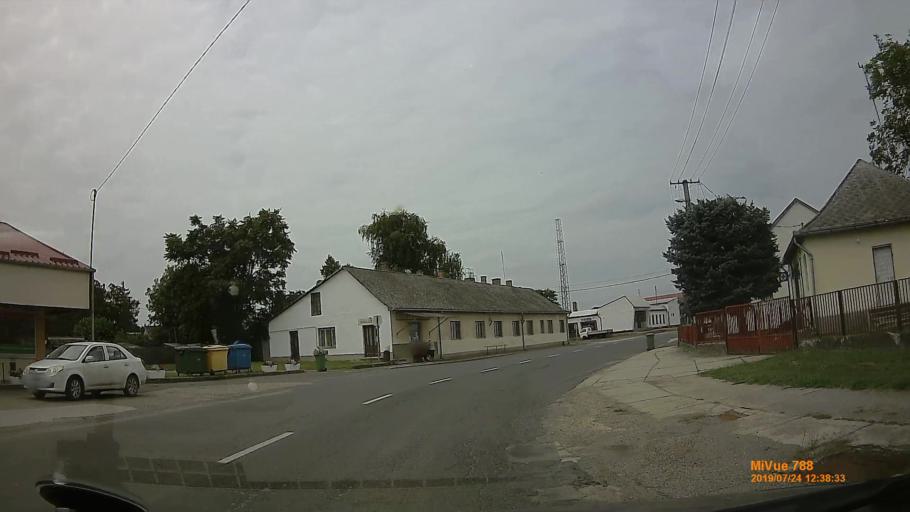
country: HU
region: Szabolcs-Szatmar-Bereg
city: Aranyosapati
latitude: 48.1865
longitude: 22.3148
